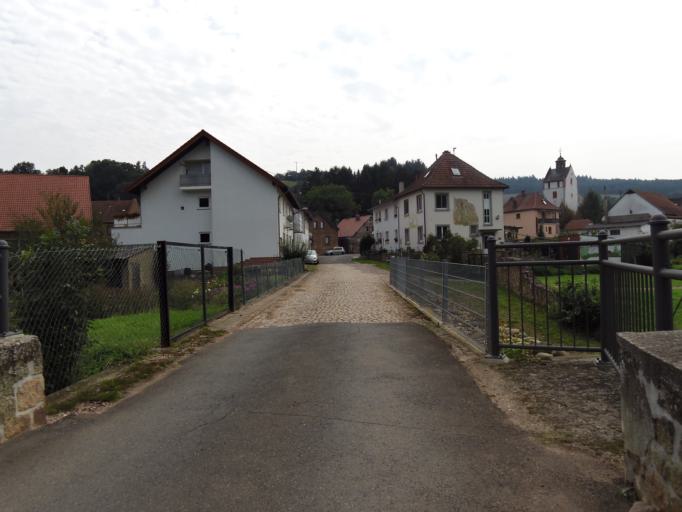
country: DE
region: Rheinland-Pfalz
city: Hochstatten
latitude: 49.7660
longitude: 7.8317
